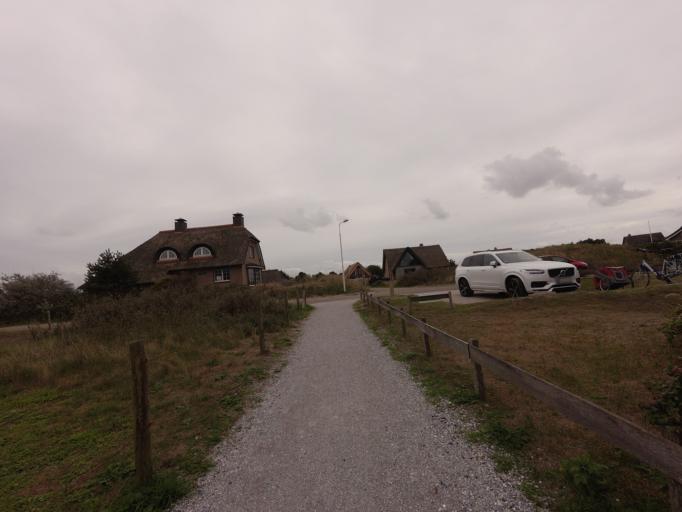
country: NL
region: Friesland
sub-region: Gemeente Ameland
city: Nes
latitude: 53.4582
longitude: 5.7955
